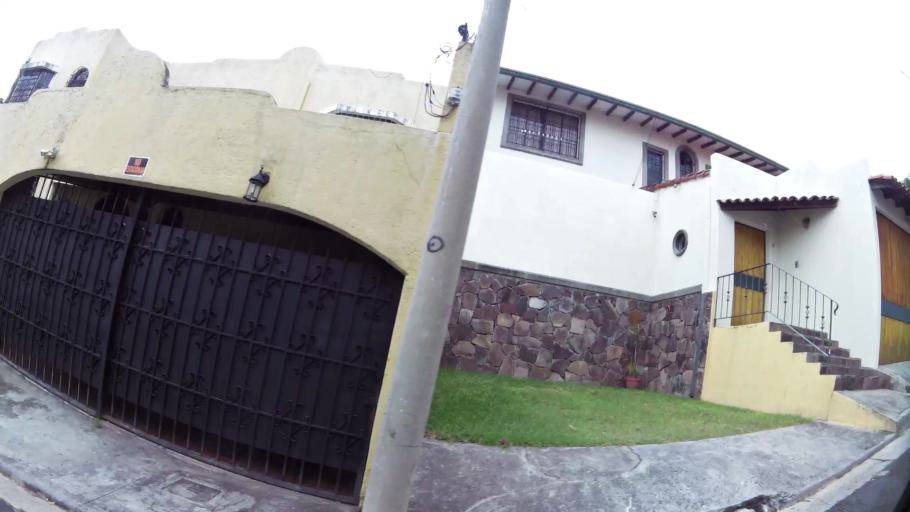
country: SV
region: San Salvador
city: Mejicanos
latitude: 13.7172
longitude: -89.2474
